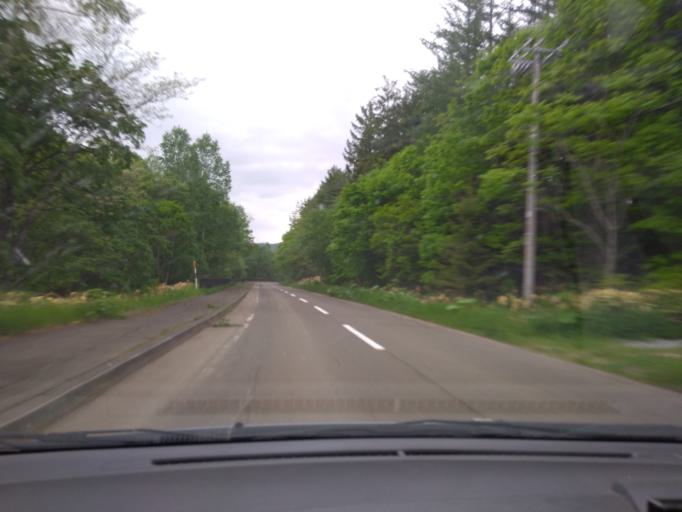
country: JP
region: Hokkaido
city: Shimo-furano
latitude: 43.1757
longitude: 142.5435
